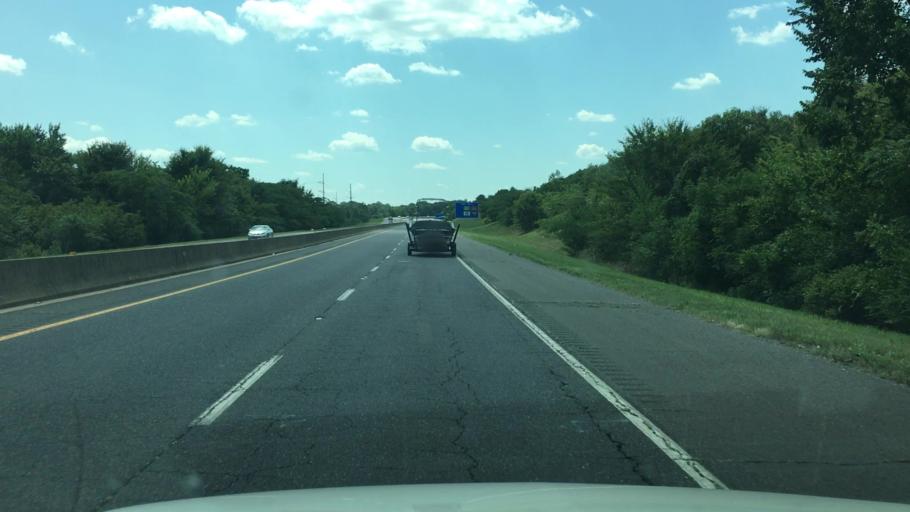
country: US
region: Arkansas
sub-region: Garland County
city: Rockwell
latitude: 34.4712
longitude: -93.1016
